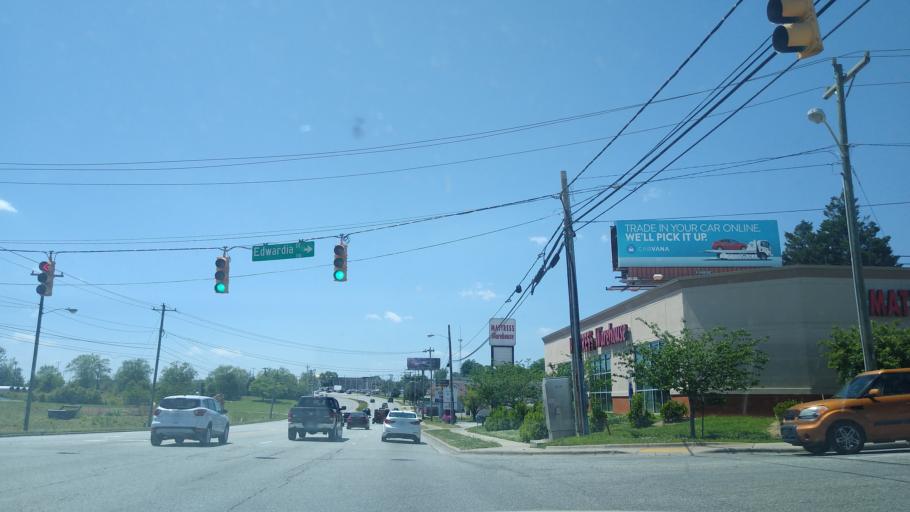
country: US
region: North Carolina
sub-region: Guilford County
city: Jamestown
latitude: 36.0598
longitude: -79.8802
